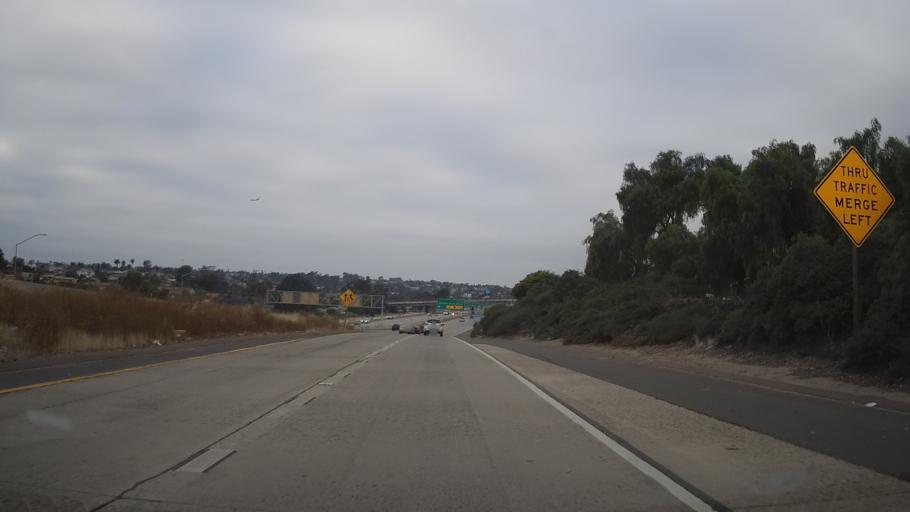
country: US
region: California
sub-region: San Diego County
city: National City
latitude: 32.6964
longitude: -117.1205
